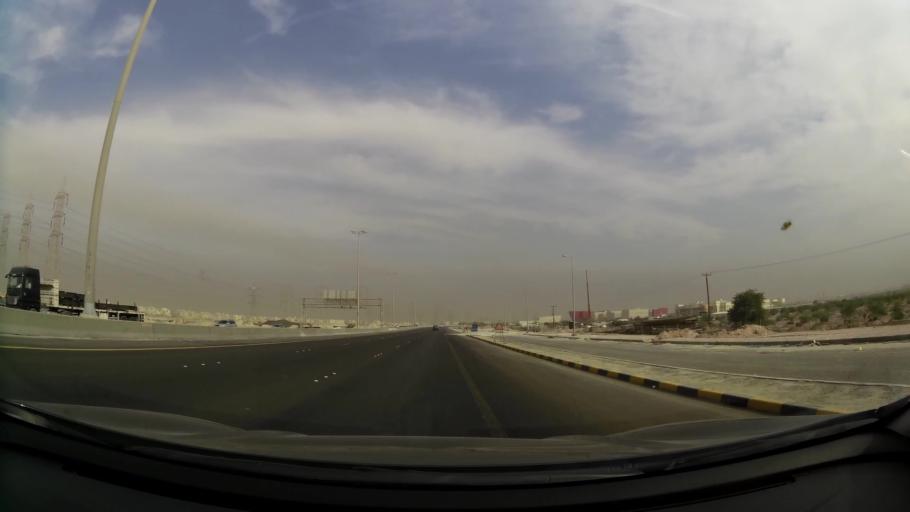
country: KW
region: Muhafazat al Jahra'
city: Al Jahra'
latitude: 29.3183
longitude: 47.7852
